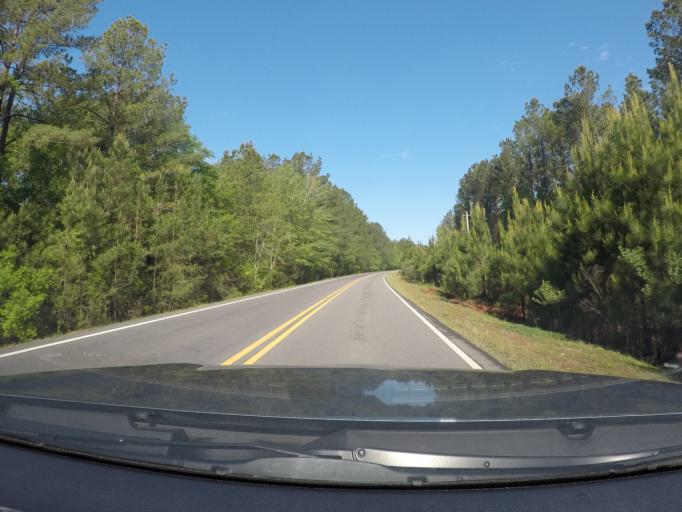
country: US
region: Georgia
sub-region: Chatham County
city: Bloomingdale
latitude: 32.0601
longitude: -81.3118
